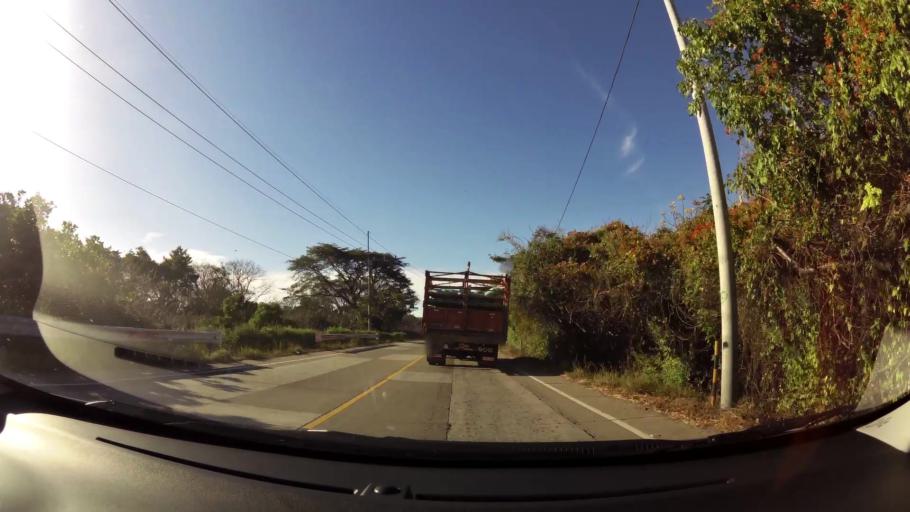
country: SV
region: Santa Ana
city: Metapan
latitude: 14.2382
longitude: -89.4708
